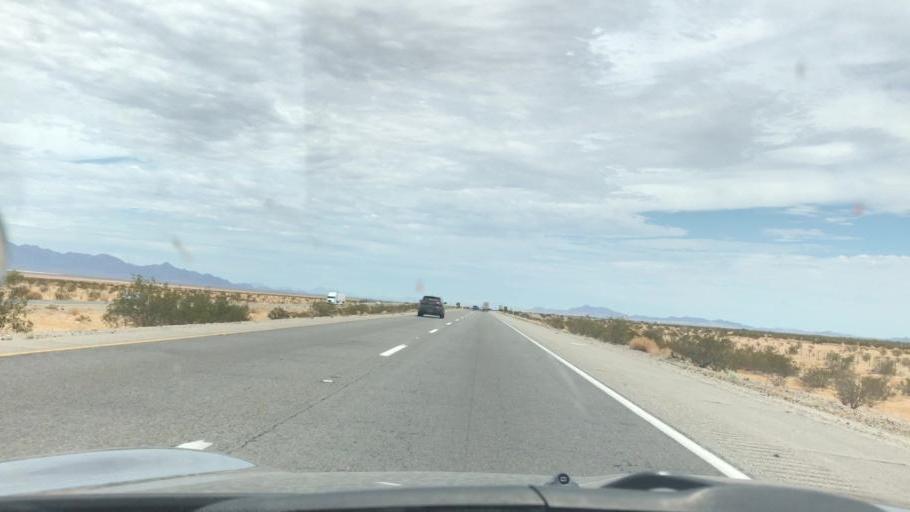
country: US
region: California
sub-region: Riverside County
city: Mesa Verde
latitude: 33.6373
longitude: -115.0882
